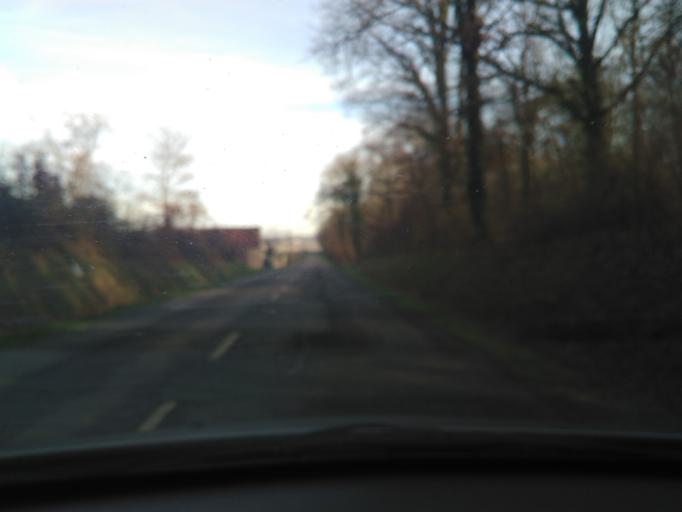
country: FR
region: Bourgogne
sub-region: Departement de la Nievre
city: Decize
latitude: 46.7822
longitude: 3.4153
